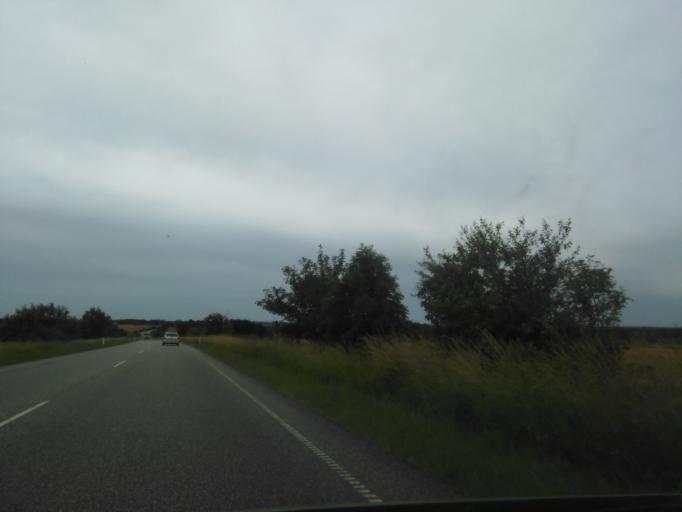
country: DK
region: Central Jutland
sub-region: Horsens Kommune
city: Horsens
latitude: 55.9042
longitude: 9.8867
